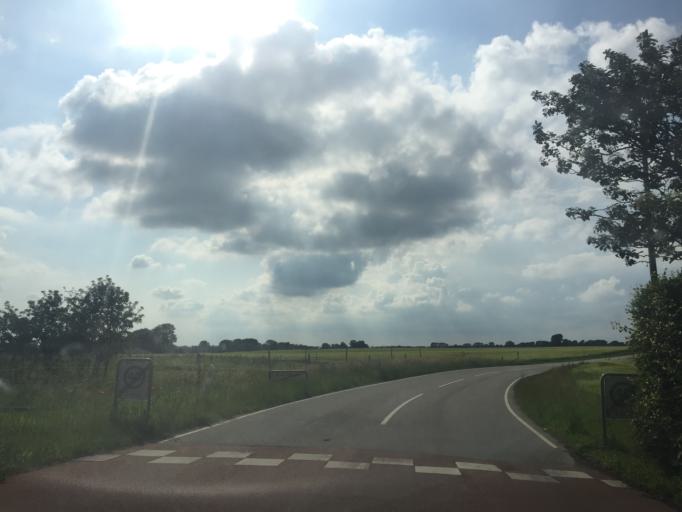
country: DK
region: Zealand
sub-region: Roskilde Kommune
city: Gundsomagle
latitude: 55.7100
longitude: 12.1586
